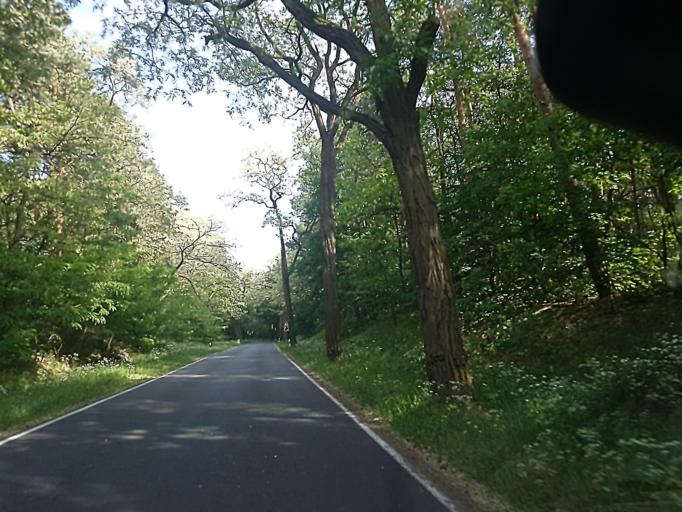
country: DE
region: Saxony-Anhalt
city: Kropstadt
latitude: 51.9838
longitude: 12.7022
